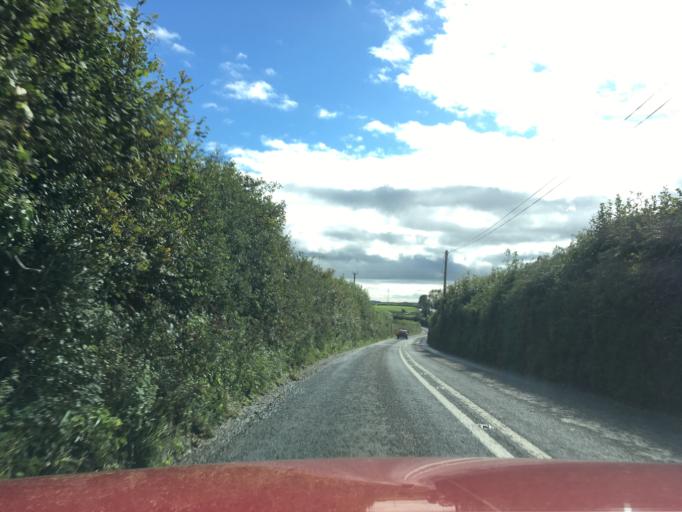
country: GB
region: England
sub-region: Devon
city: Kingsbridge
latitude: 50.3417
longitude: -3.7372
